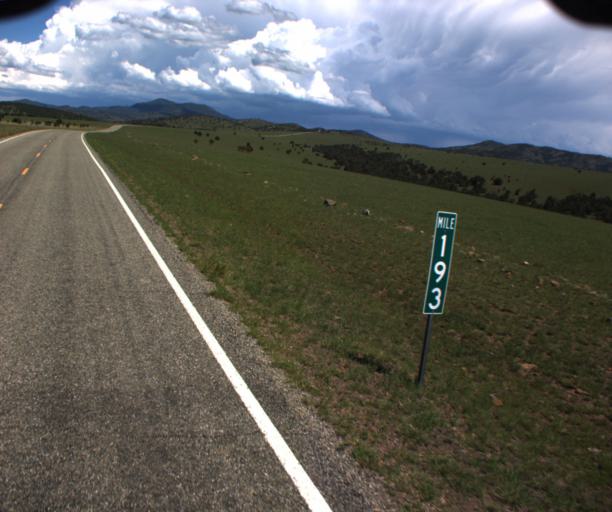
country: US
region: Arizona
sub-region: Greenlee County
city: Morenci
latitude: 33.3172
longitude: -109.3501
